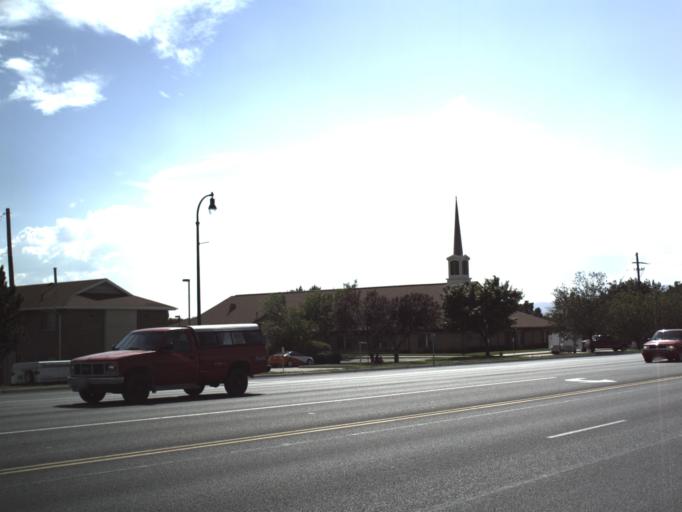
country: US
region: Utah
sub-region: Utah County
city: Orem
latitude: 40.3122
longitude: -111.7125
